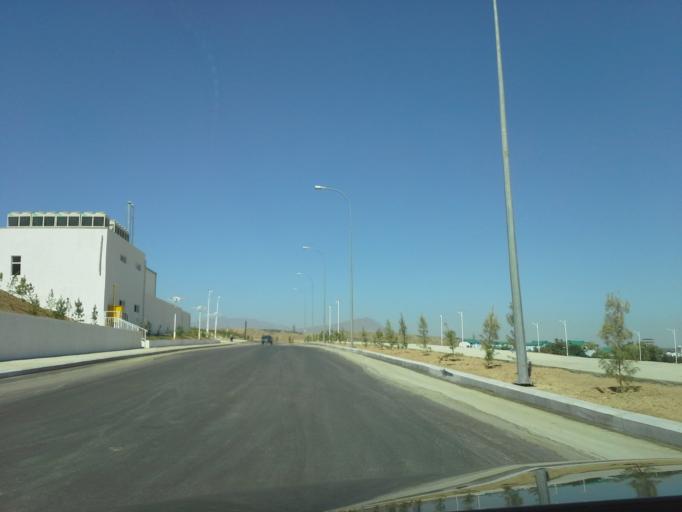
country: TM
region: Ahal
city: Ashgabat
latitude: 37.9432
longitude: 58.3471
